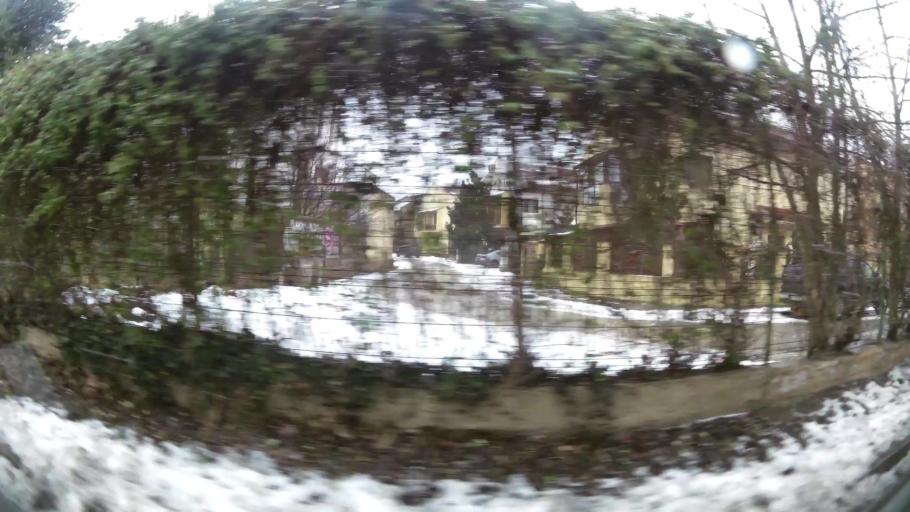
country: RO
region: Ilfov
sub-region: Comuna Mogosoaia
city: Mogosoaia
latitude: 44.4997
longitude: 26.0396
